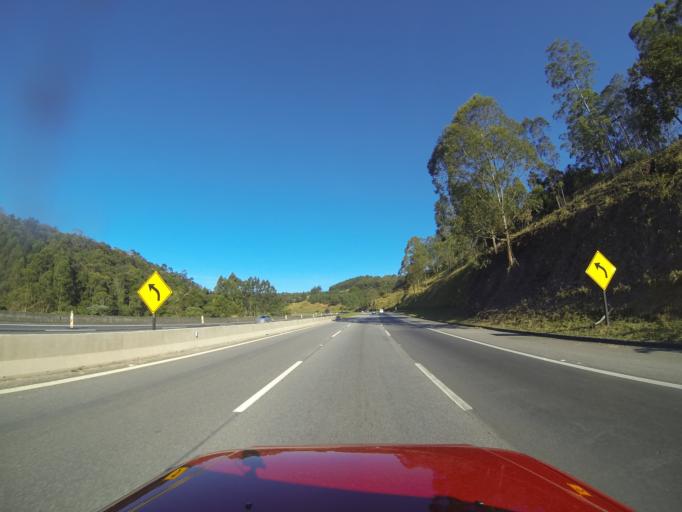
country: BR
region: Sao Paulo
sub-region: Piracaia
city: Piracaia
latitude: -23.1799
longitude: -46.3121
